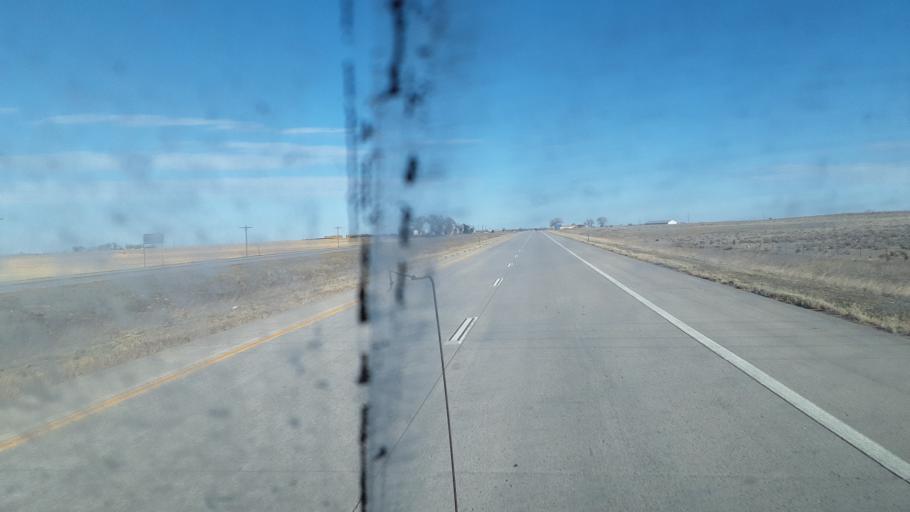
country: US
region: Colorado
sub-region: Morgan County
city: Fort Morgan
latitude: 40.2321
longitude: -104.1133
